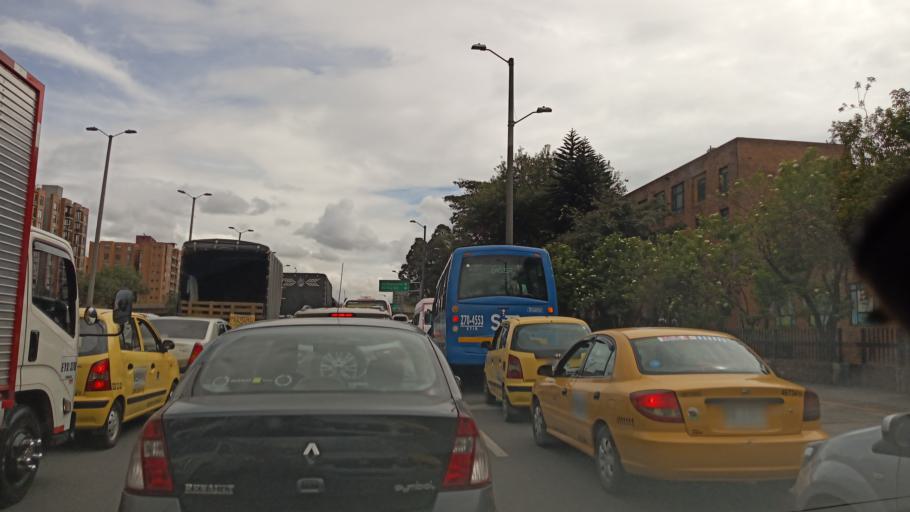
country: CO
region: Bogota D.C.
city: Bogota
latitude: 4.6601
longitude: -74.1168
